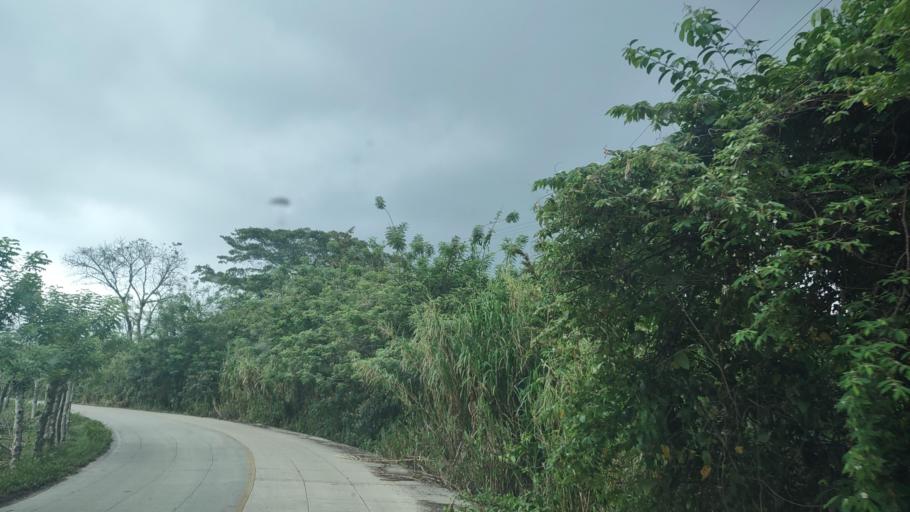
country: MX
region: Veracruz
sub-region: Uxpanapa
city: Poblado 10
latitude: 17.4924
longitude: -94.1766
